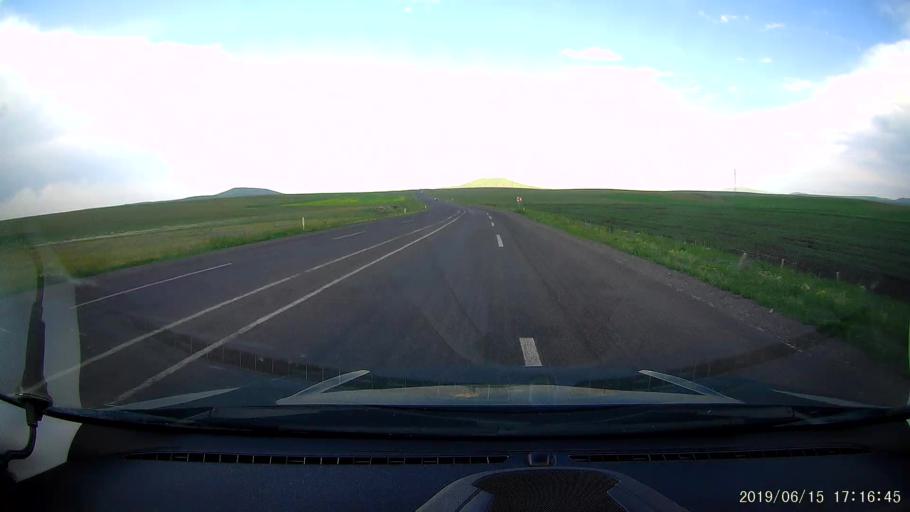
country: TR
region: Kars
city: Kars
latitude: 40.6143
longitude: 43.2239
